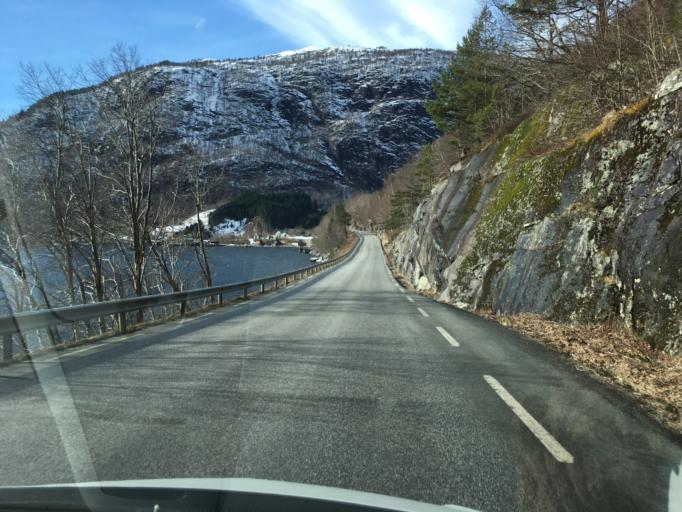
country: NO
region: Hordaland
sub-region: Granvin
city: Granvin
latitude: 60.4748
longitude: 6.6225
